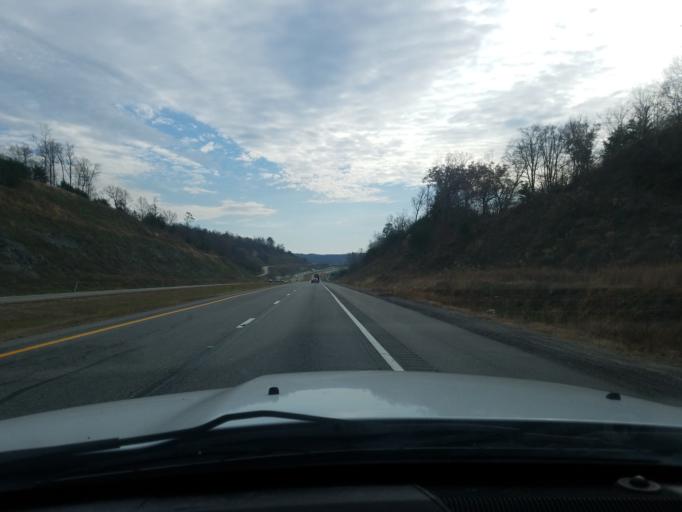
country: US
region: West Virginia
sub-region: Putnam County
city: Teays Valley
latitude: 38.4667
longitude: -81.9091
